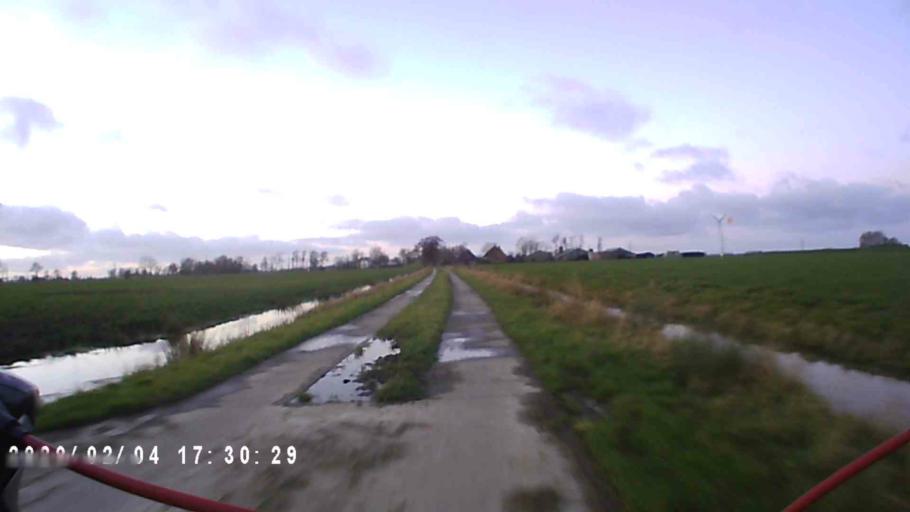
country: NL
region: Groningen
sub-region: Gemeente Zuidhorn
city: Aduard
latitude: 53.2753
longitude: 6.5014
